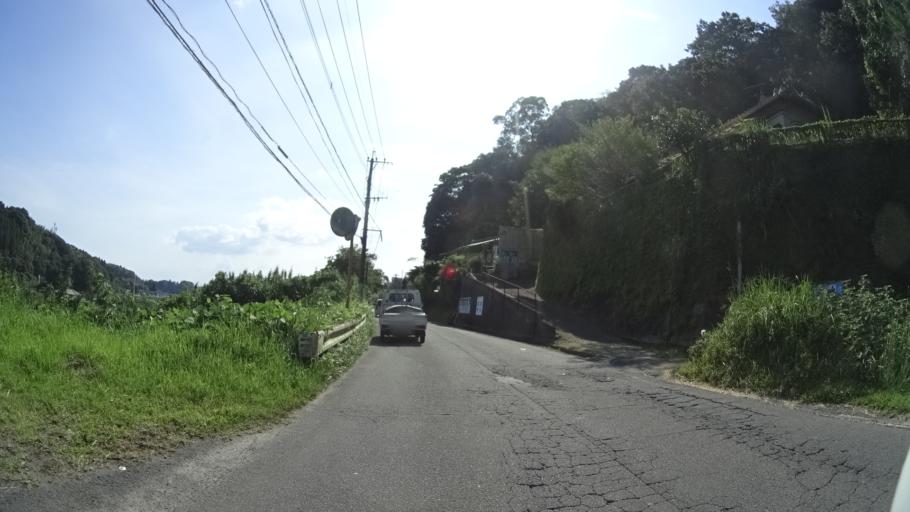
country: JP
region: Kagoshima
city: Kagoshima-shi
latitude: 31.6642
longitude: 130.5543
